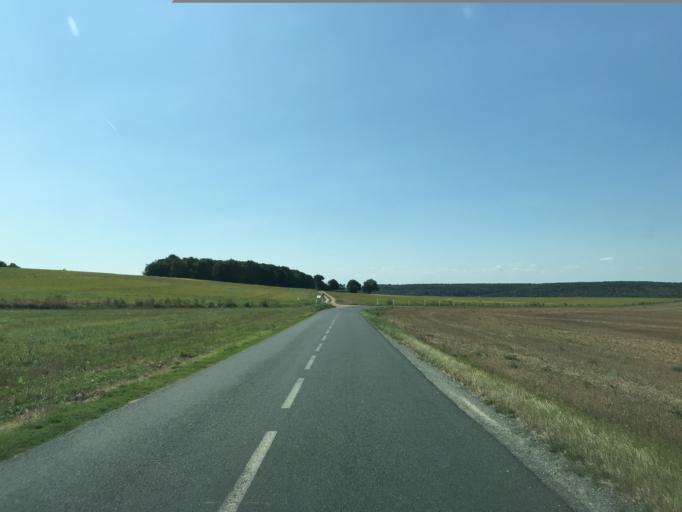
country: FR
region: Haute-Normandie
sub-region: Departement de l'Eure
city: Houlbec-Cocherel
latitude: 49.0834
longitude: 1.3215
